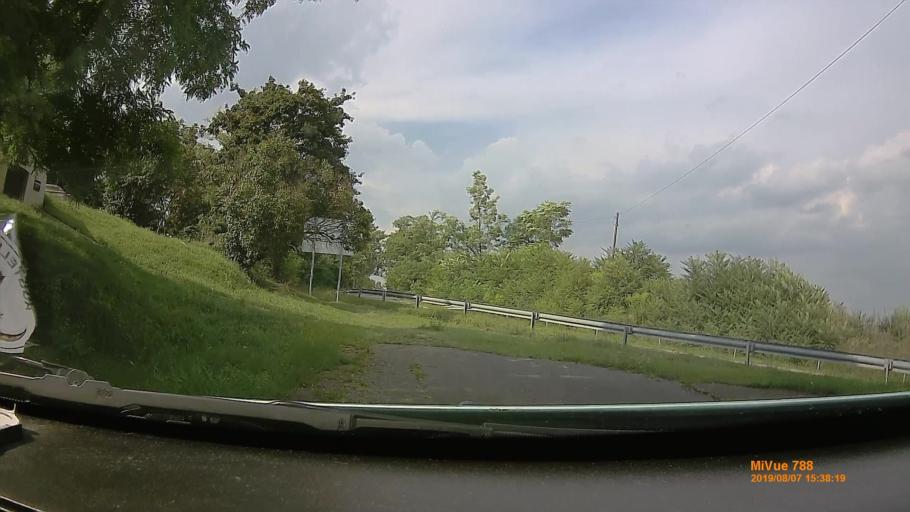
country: HU
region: Borsod-Abauj-Zemplen
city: Encs
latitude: 48.4224
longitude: 21.1757
